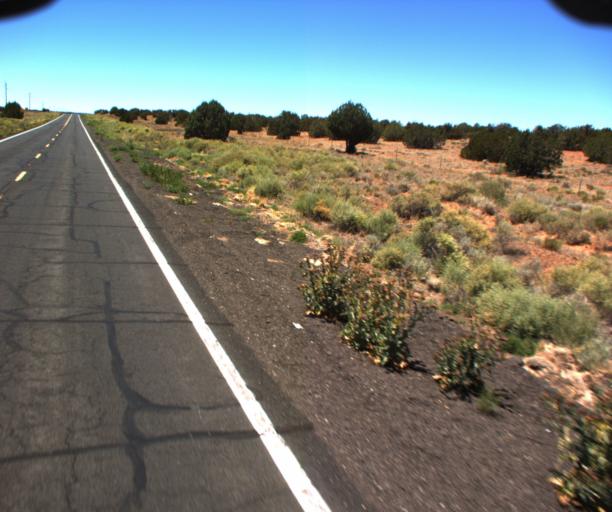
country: US
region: Arizona
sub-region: Coconino County
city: LeChee
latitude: 34.8545
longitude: -110.9228
